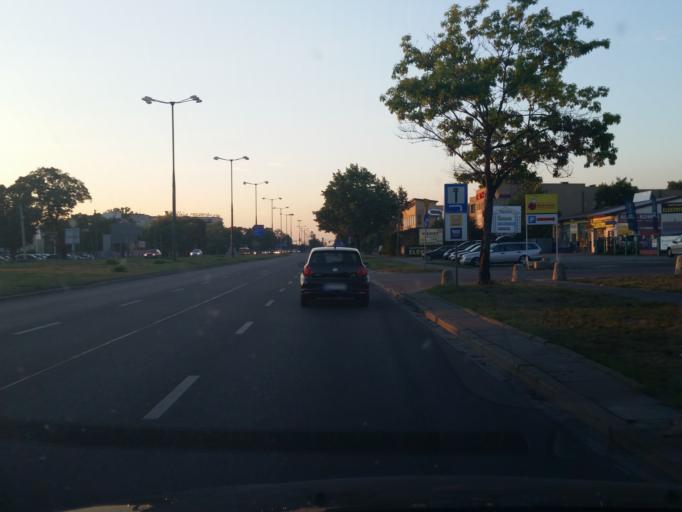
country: PL
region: Masovian Voivodeship
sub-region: Warszawa
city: Bialoleka
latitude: 52.3183
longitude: 20.9741
